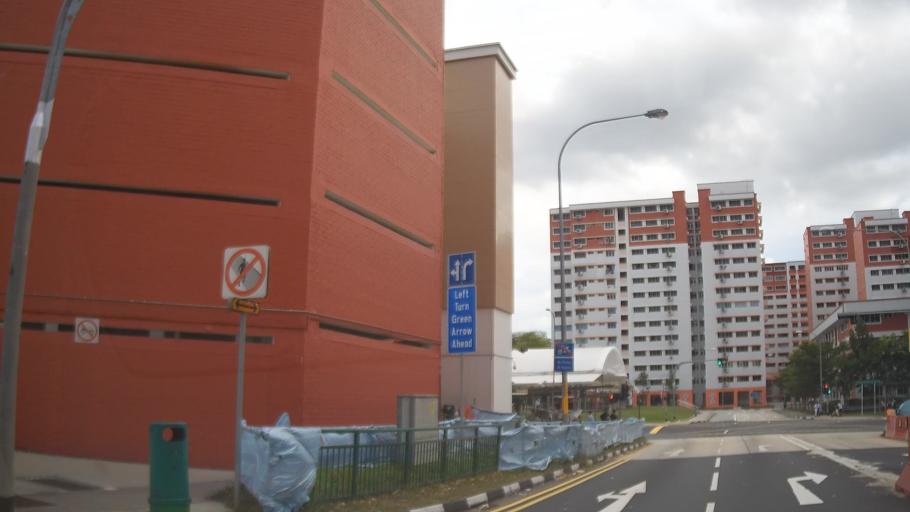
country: MY
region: Johor
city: Johor Bahru
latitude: 1.3846
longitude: 103.7434
